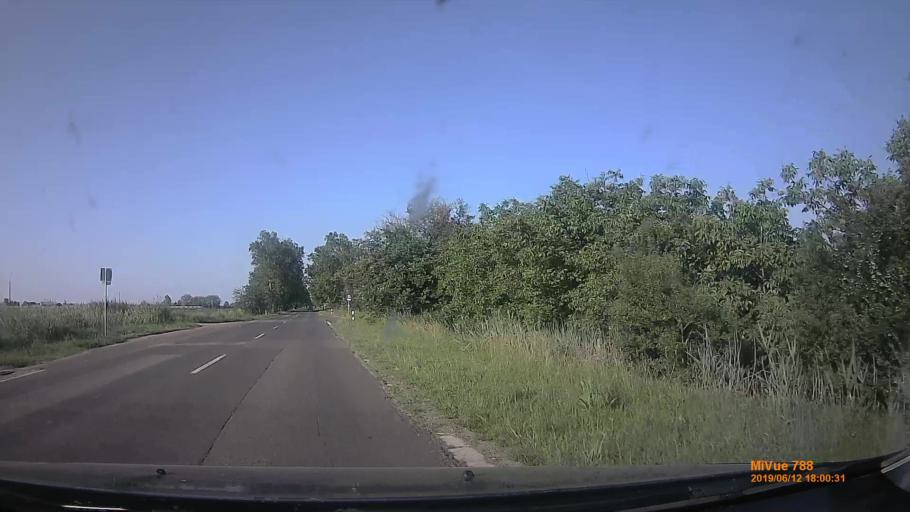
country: HU
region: Csongrad
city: Roszke
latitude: 46.2177
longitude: 20.0624
